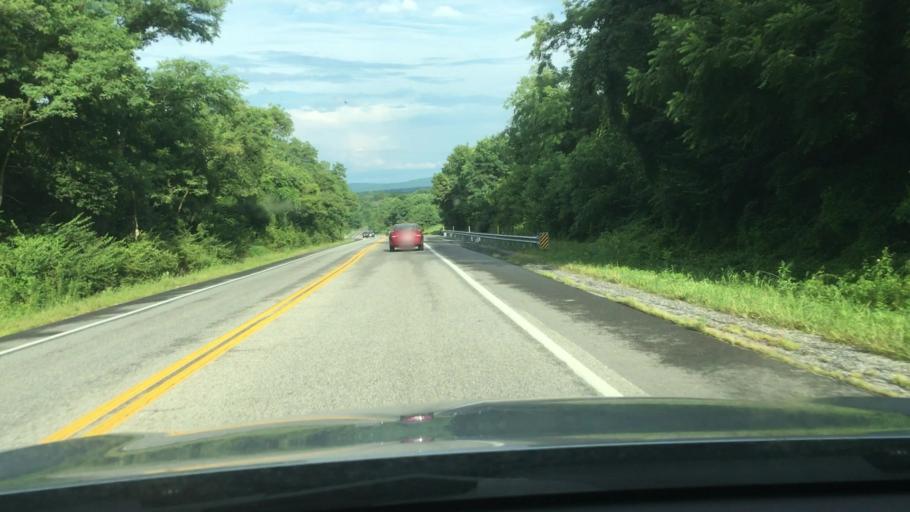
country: US
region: Pennsylvania
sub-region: York County
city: Dillsburg
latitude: 40.0967
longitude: -76.9688
